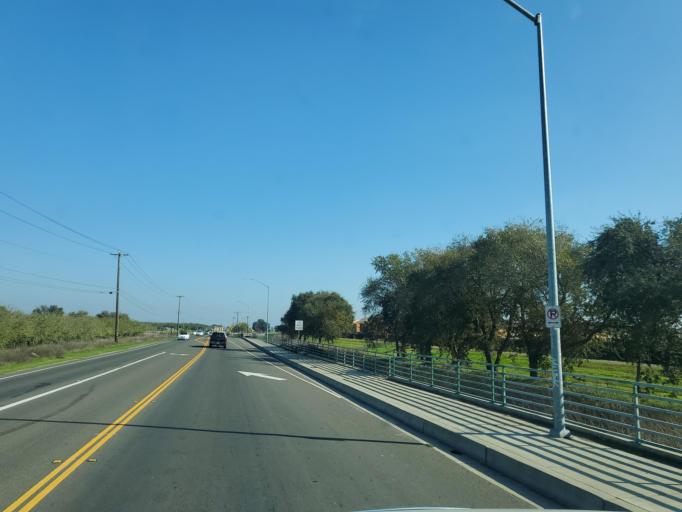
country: US
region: California
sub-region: San Joaquin County
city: Lincoln Village
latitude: 38.0576
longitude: -121.3172
